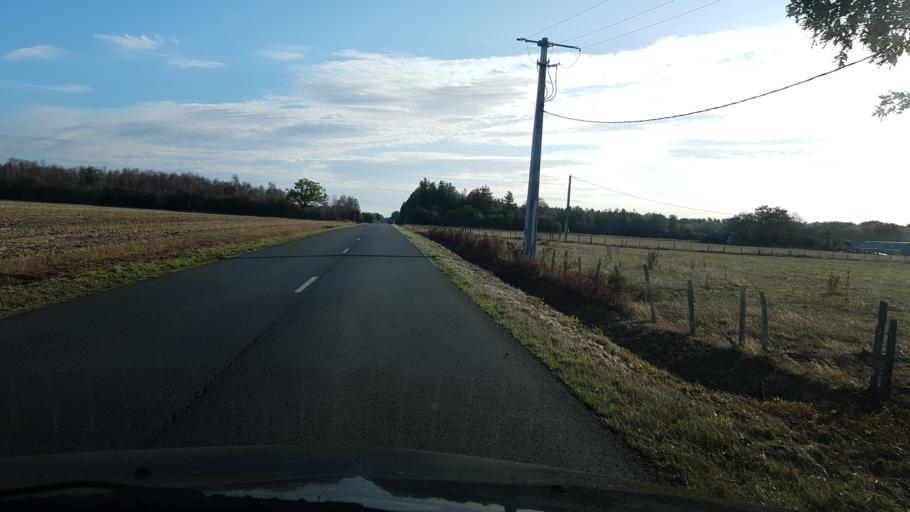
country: FR
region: Centre
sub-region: Departement du Cher
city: Brinon-sur-Sauldre
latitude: 47.6565
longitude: 2.2057
